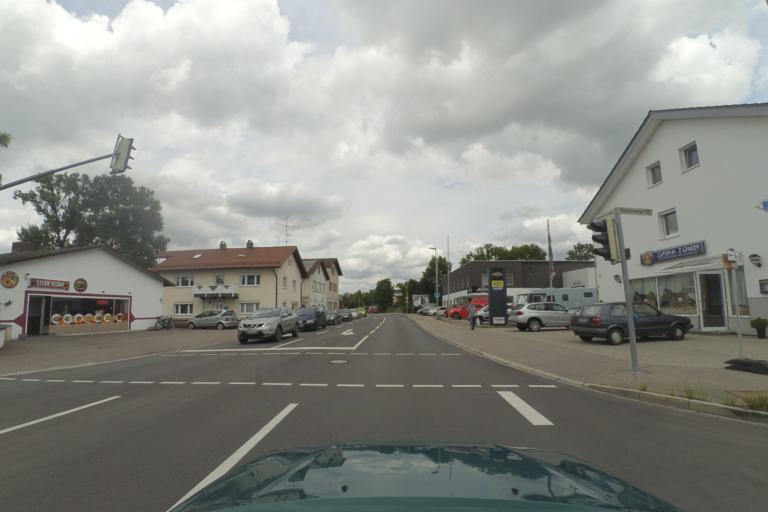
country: DE
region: Bavaria
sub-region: Lower Bavaria
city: Dingolfing
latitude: 48.6365
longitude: 12.4956
